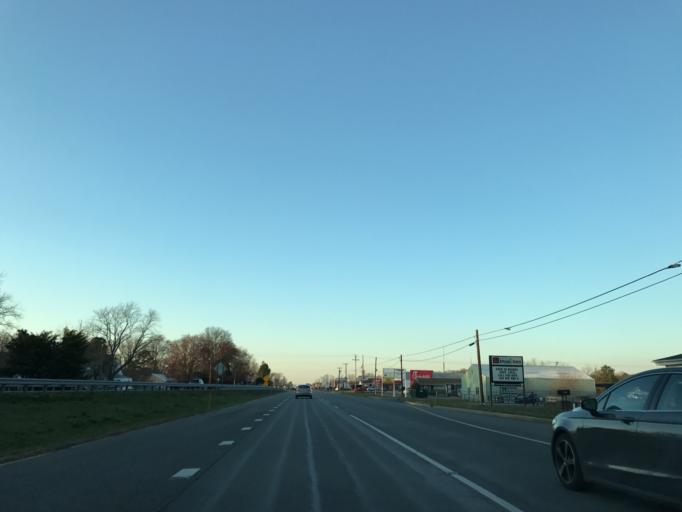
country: US
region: Maryland
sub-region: Talbot County
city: Easton
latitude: 38.8020
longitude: -76.0600
